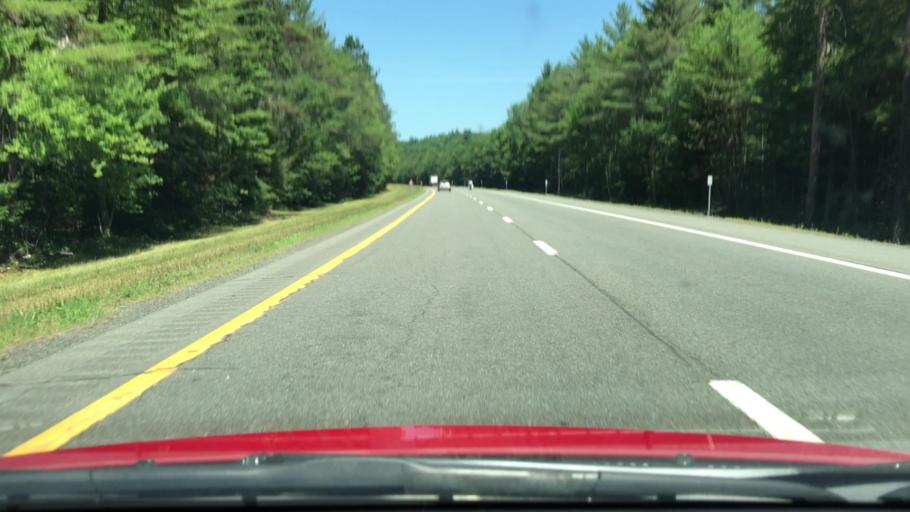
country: US
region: New York
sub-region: Essex County
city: Elizabethtown
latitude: 44.3180
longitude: -73.5280
